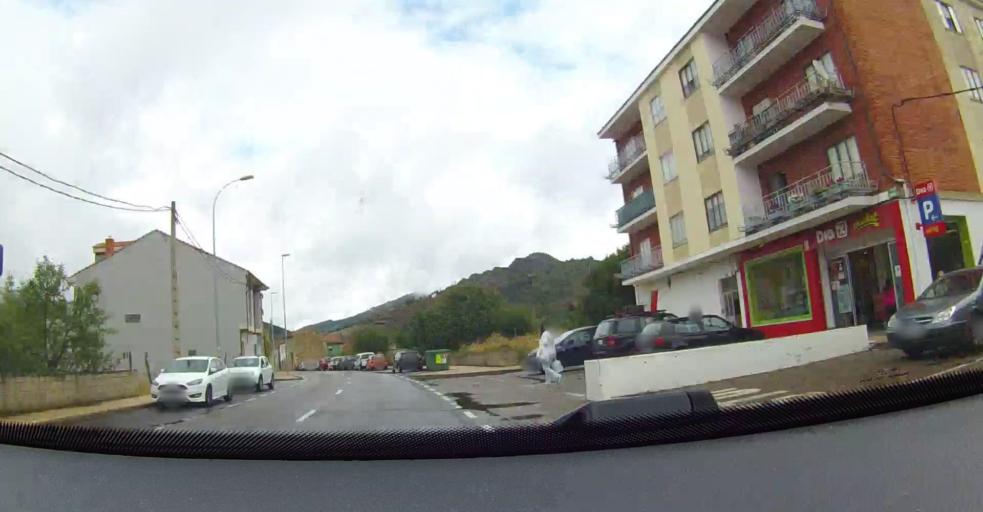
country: ES
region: Castille and Leon
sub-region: Provincia de Leon
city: Bonar
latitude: 42.8683
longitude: -5.3232
